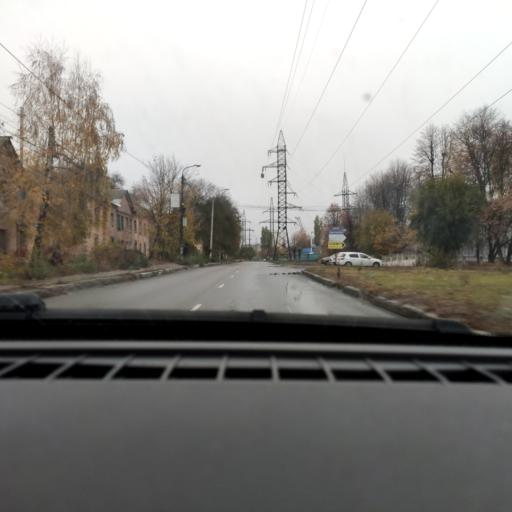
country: RU
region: Voronezj
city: Voronezh
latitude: 51.6940
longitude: 39.2085
